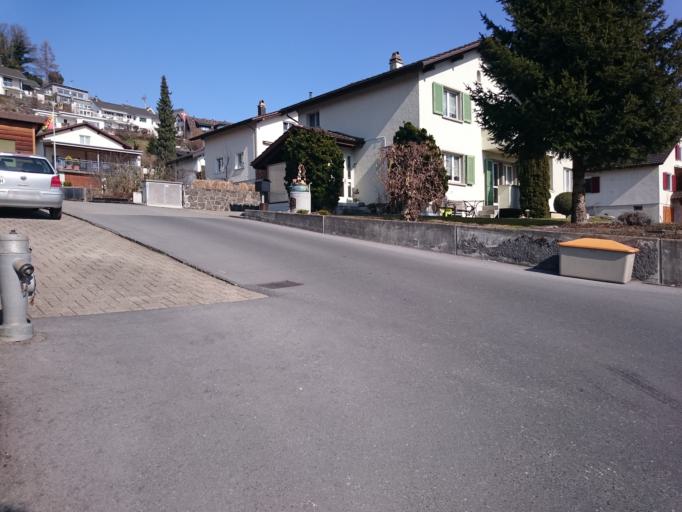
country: CH
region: Saint Gallen
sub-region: Wahlkreis See-Gaster
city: Uznach
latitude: 47.2243
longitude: 8.9952
